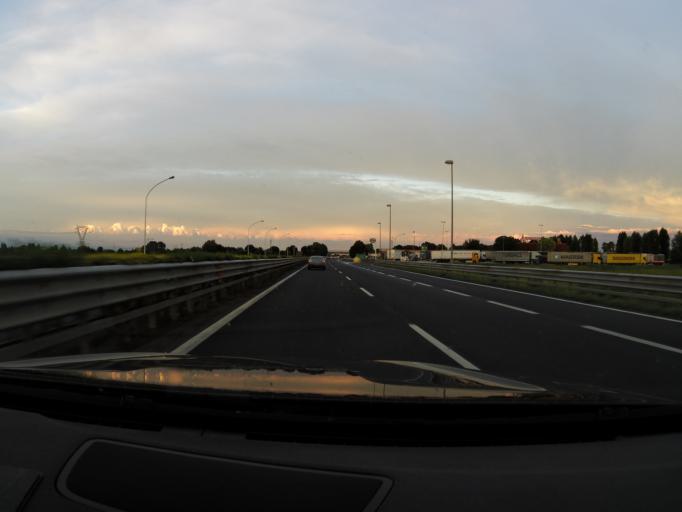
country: IT
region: Veneto
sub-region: Provincia di Venezia
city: Teglio Veneto
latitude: 45.8045
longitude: 12.8843
